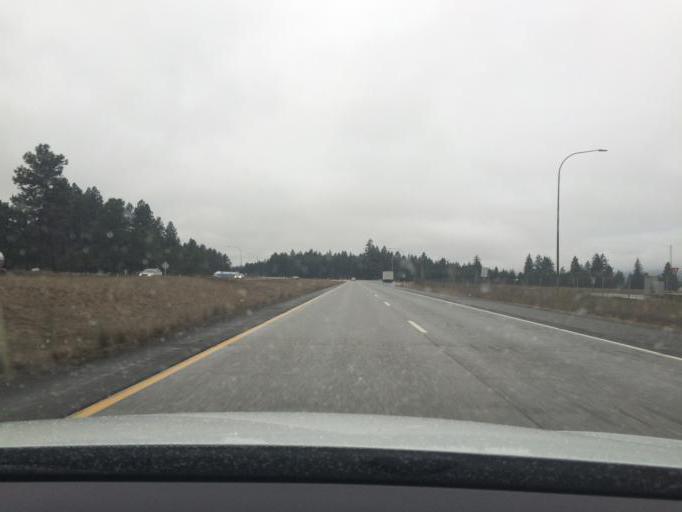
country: US
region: Washington
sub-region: Kittitas County
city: Cle Elum
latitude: 47.1609
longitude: -120.8442
